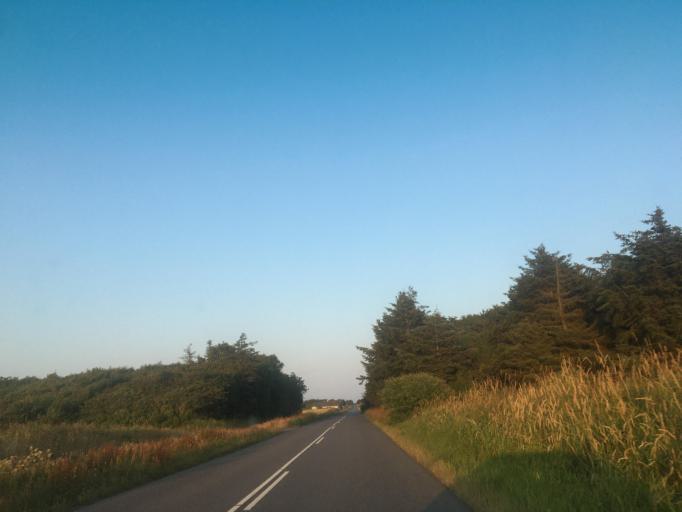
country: DK
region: North Denmark
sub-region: Thisted Kommune
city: Hurup
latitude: 56.7574
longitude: 8.3527
